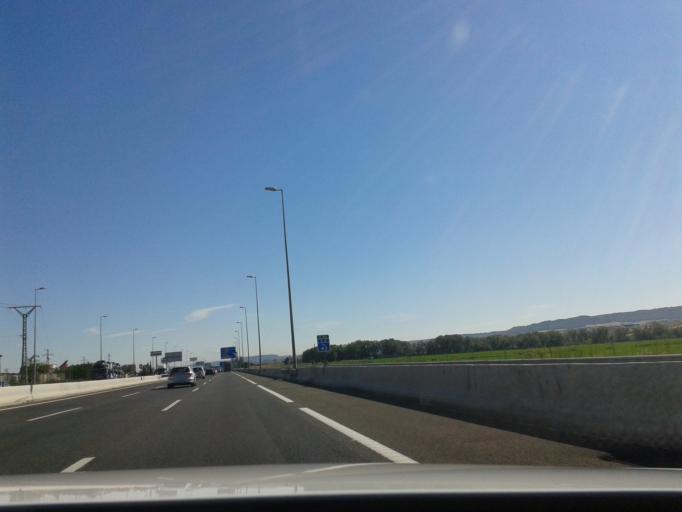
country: ES
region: Castille-La Mancha
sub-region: Provincia de Guadalajara
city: Azuqueca de Henares
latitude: 40.5606
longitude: -3.2565
